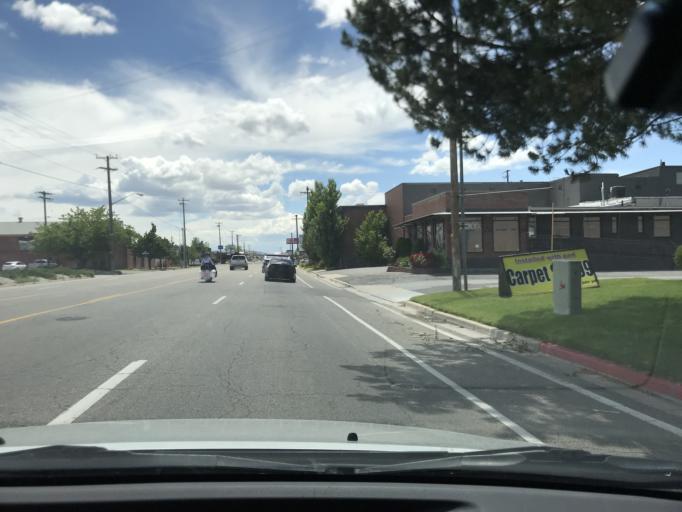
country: US
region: Utah
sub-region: Salt Lake County
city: South Salt Lake
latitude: 40.7082
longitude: -111.8998
